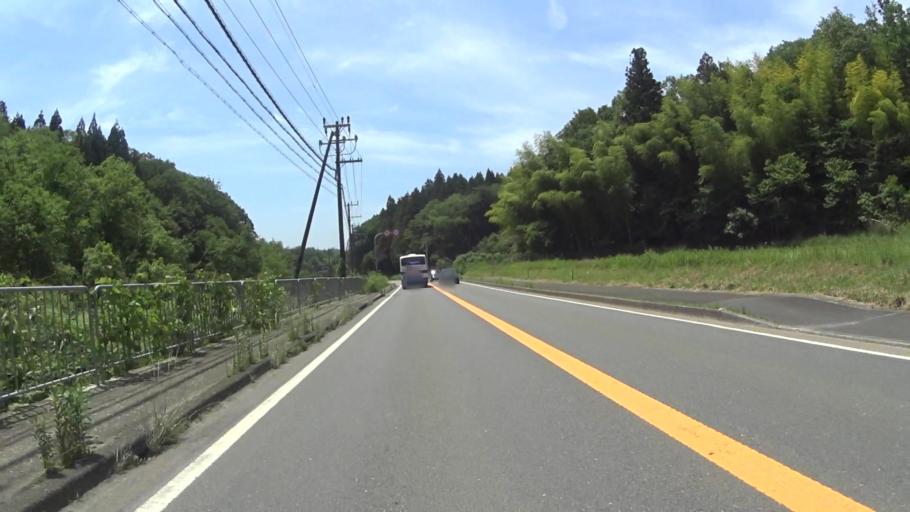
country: JP
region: Kyoto
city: Ayabe
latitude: 35.1792
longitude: 135.3569
